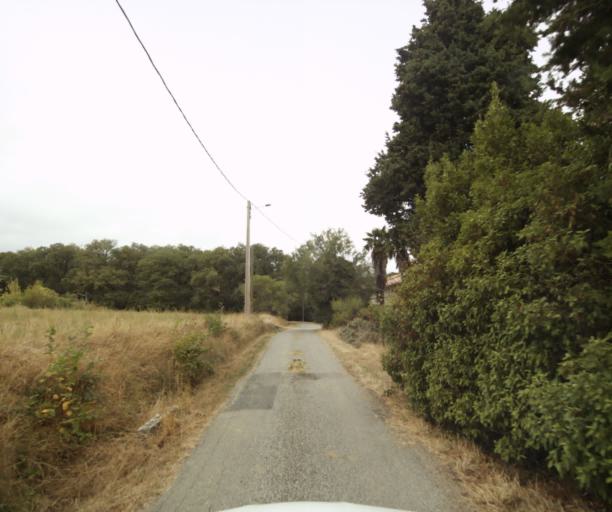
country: FR
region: Midi-Pyrenees
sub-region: Departement de la Haute-Garonne
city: Villefranche-de-Lauragais
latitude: 43.4146
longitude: 1.7445
